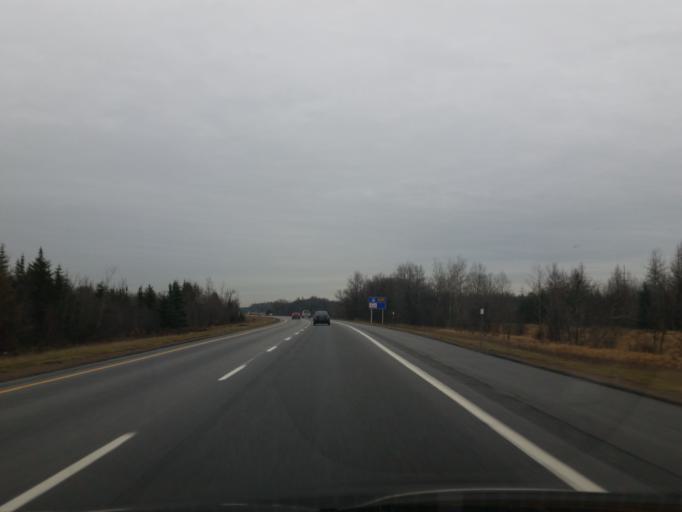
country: CA
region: Quebec
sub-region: Capitale-Nationale
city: Saint-Augustin-de-Desmaures
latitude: 46.7512
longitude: -71.4961
